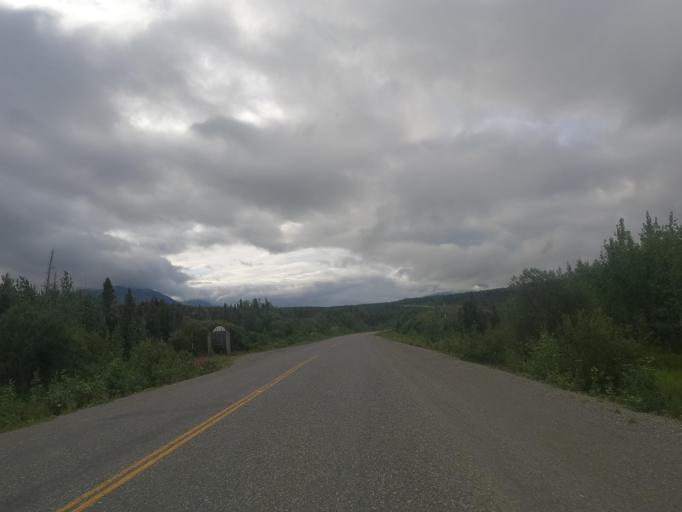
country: CA
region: Yukon
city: Haines Junction
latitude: 59.9991
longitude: -136.8470
